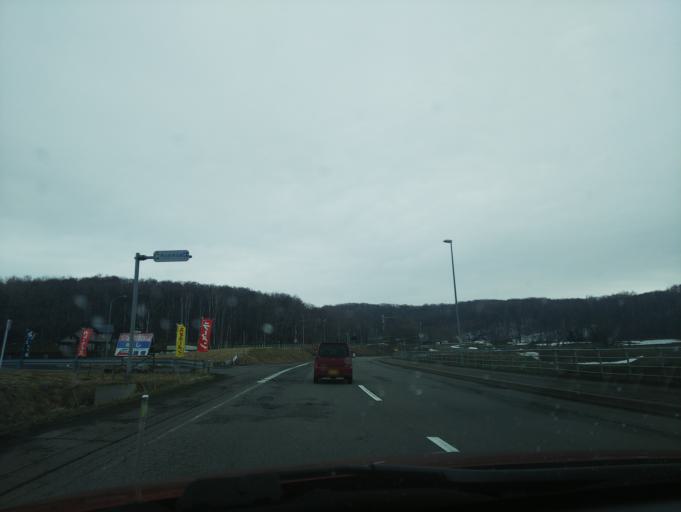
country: JP
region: Hokkaido
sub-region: Asahikawa-shi
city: Asahikawa
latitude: 43.8470
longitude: 142.4477
